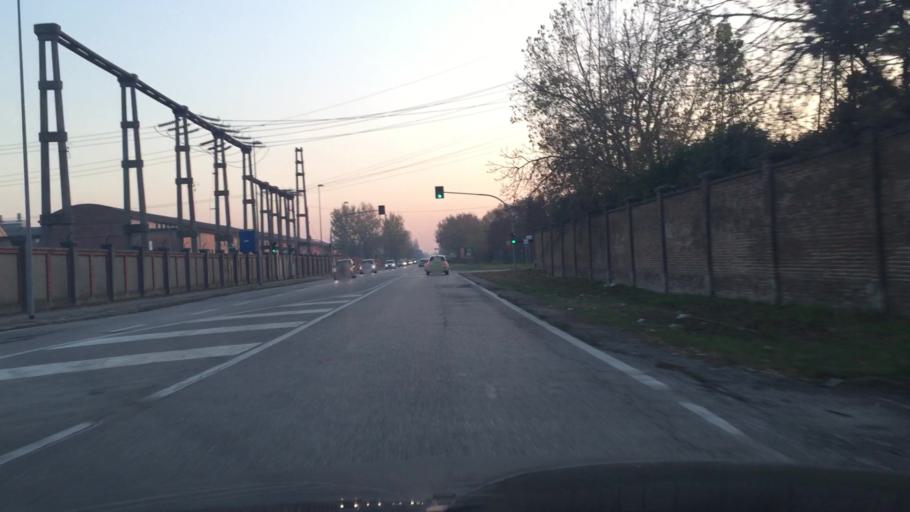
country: IT
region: Emilia-Romagna
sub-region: Provincia di Ferrara
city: Ferrara
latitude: 44.8587
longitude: 11.6013
